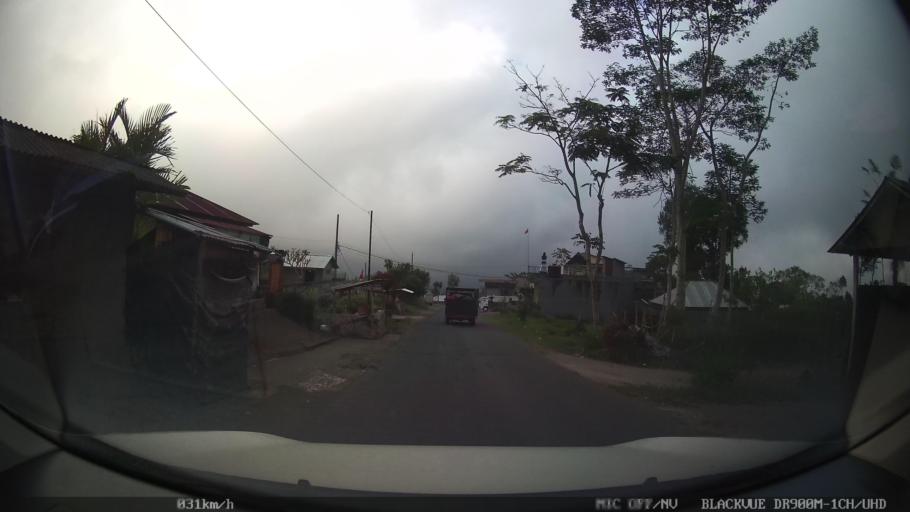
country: ID
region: Bali
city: Banjar Kedisan
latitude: -8.2676
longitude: 115.3309
